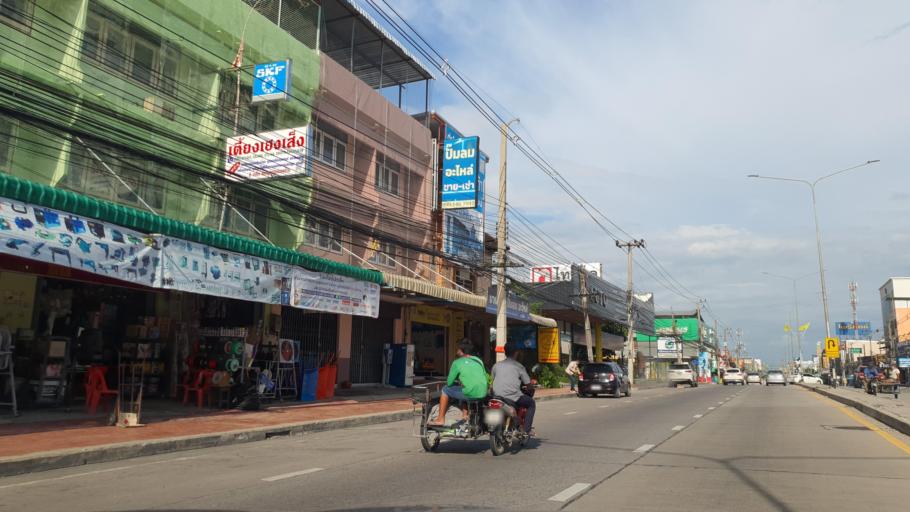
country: TH
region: Chon Buri
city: Chon Buri
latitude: 13.3574
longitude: 100.9957
